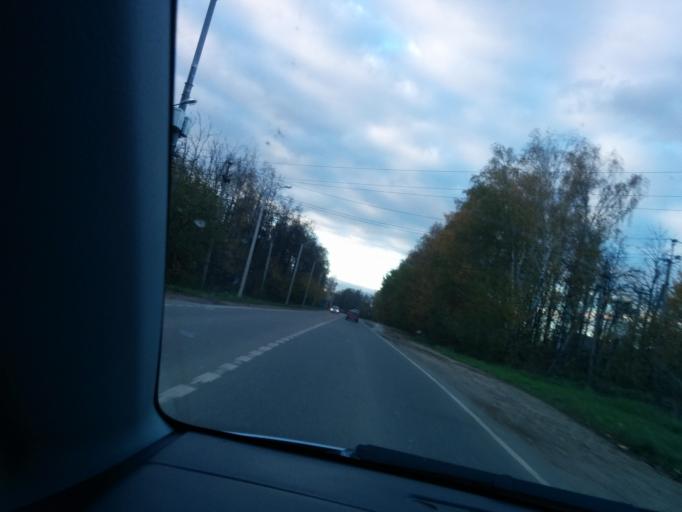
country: RU
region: Moscow
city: Zagor'ye
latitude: 55.5314
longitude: 37.6537
